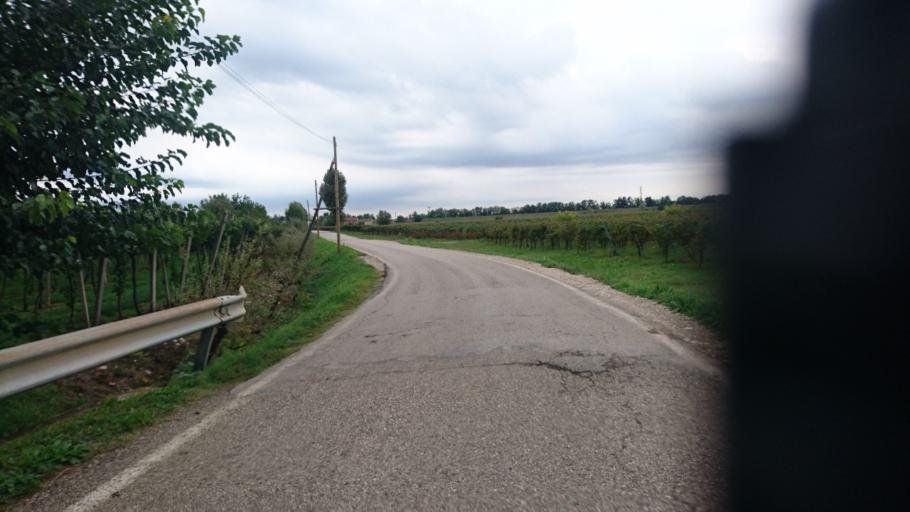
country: IT
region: Veneto
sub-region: Provincia di Vicenza
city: Gambellara
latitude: 45.4382
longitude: 11.3391
